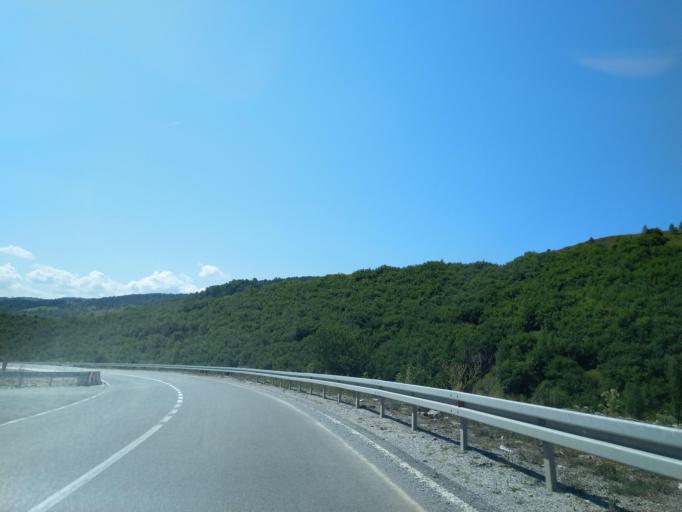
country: RS
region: Central Serbia
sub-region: Zlatiborski Okrug
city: Sjenica
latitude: 43.2971
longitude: 19.9363
